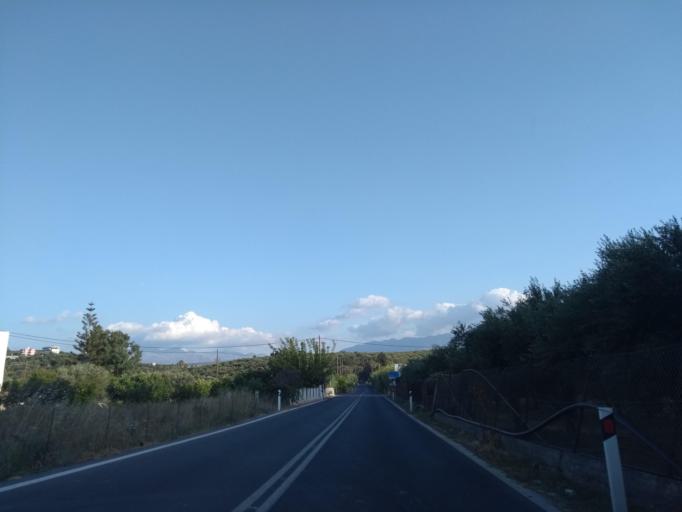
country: GR
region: Crete
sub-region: Nomos Chanias
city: Kalivai
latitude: 35.4623
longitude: 24.1534
